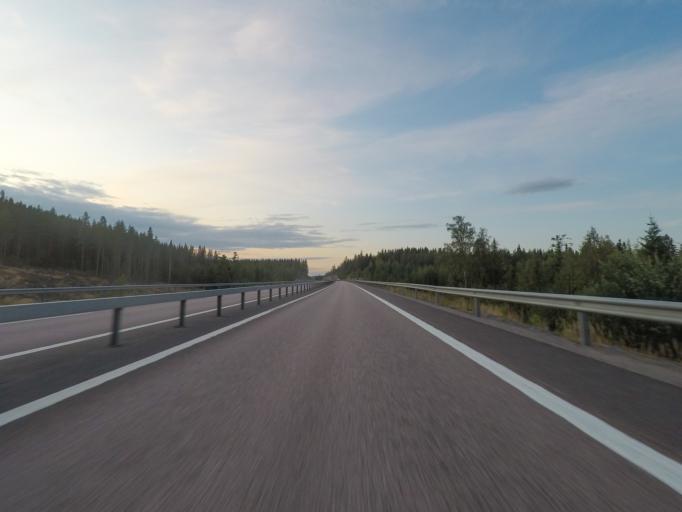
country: FI
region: Central Finland
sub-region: Jyvaeskylae
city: Saeynaetsalo
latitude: 62.1764
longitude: 25.9066
